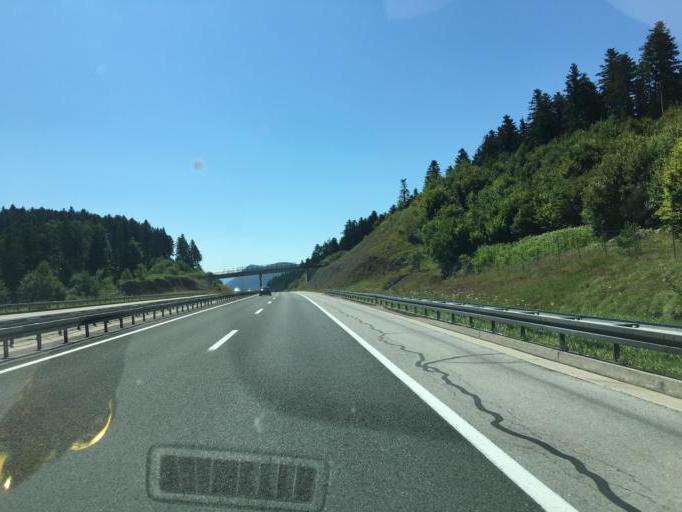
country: HR
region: Licko-Senjska
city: Otocac
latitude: 44.8510
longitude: 15.2295
